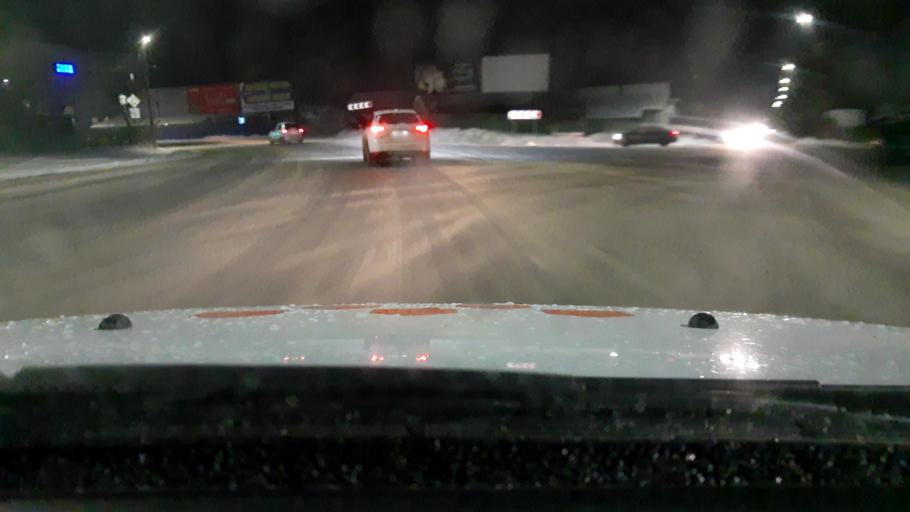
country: RU
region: Nizjnij Novgorod
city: Gorodets
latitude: 56.6581
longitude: 43.4707
